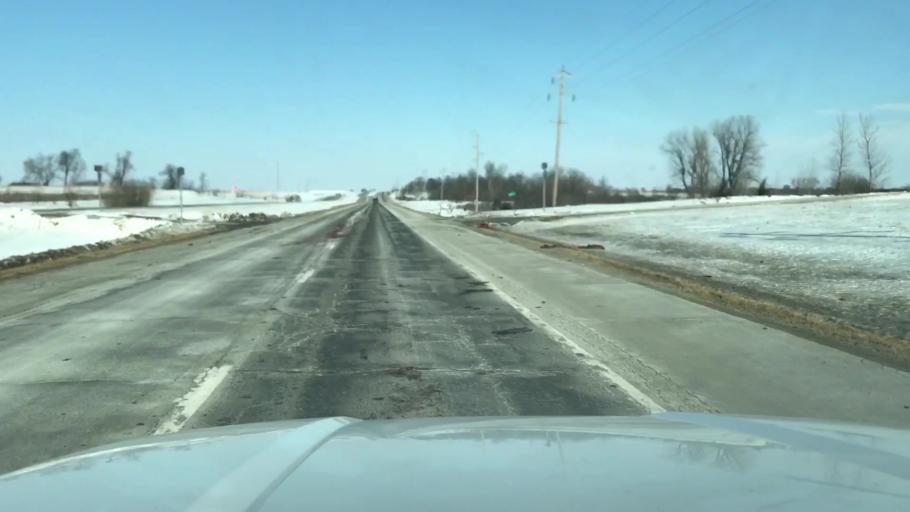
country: US
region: Missouri
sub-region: Nodaway County
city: Maryville
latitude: 40.2113
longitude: -94.8678
